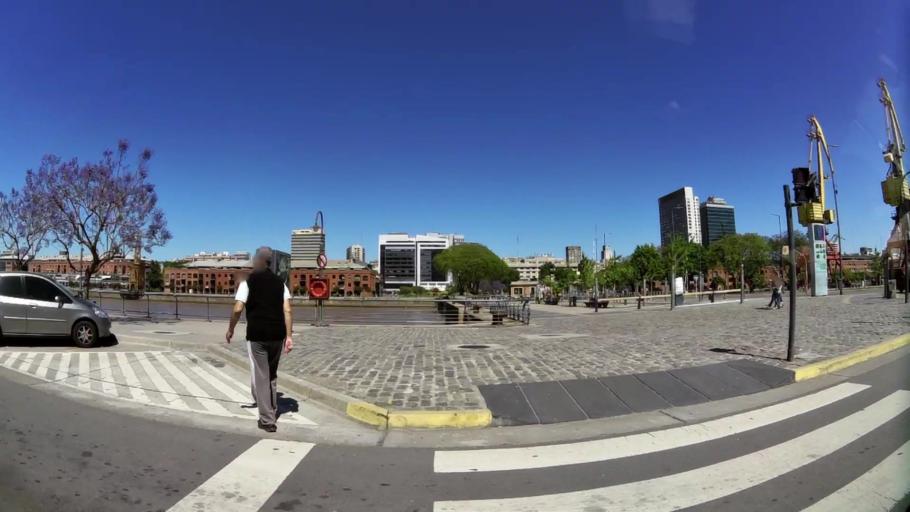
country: AR
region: Buenos Aires F.D.
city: Buenos Aires
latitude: -34.6181
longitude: -58.3628
